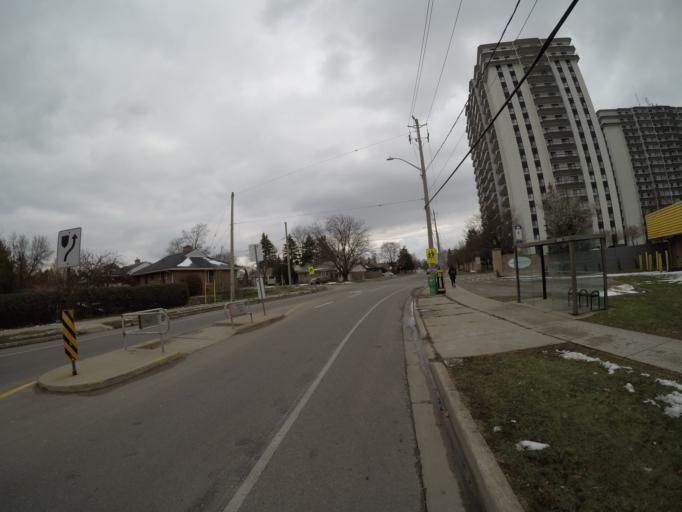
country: CA
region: Ontario
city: Waterloo
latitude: 43.4652
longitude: -80.4966
